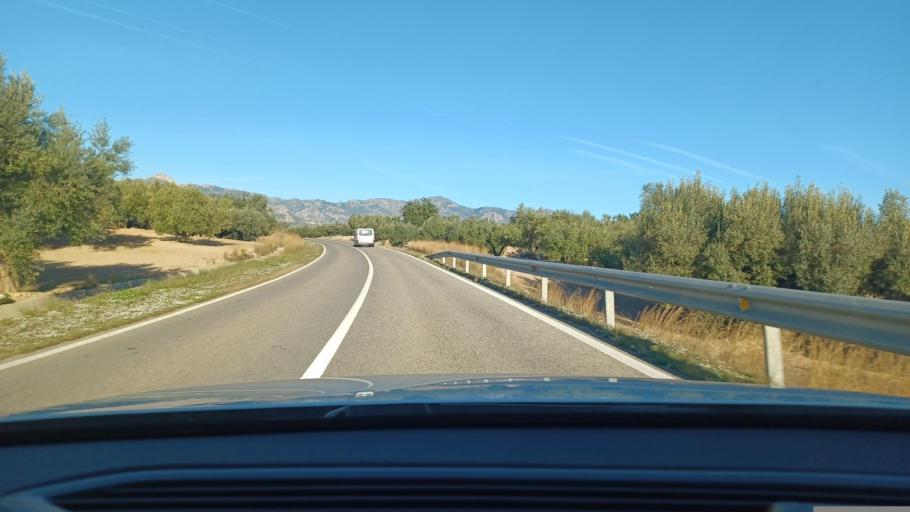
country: ES
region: Catalonia
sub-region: Provincia de Tarragona
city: Mas de Barberans
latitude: 40.7165
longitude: 0.4022
